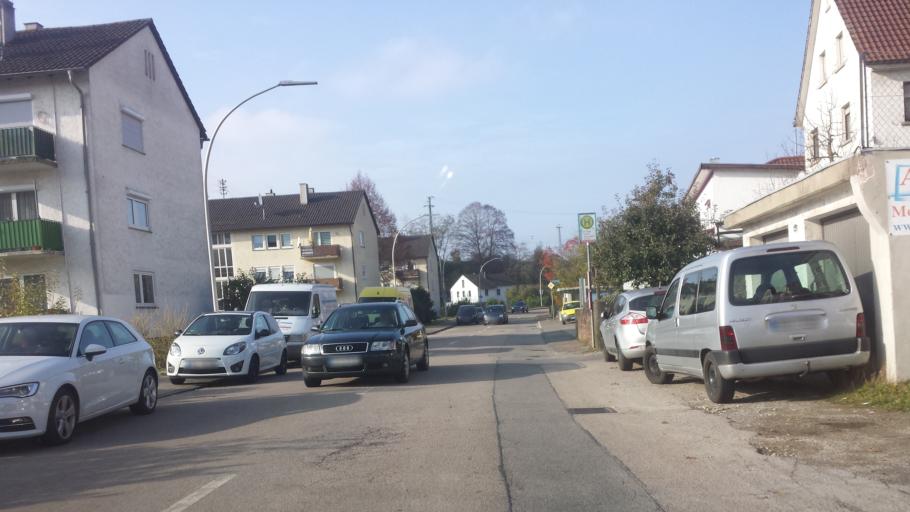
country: DE
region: Baden-Wuerttemberg
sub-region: Karlsruhe Region
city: Neckarzimmern
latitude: 49.3445
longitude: 9.1190
